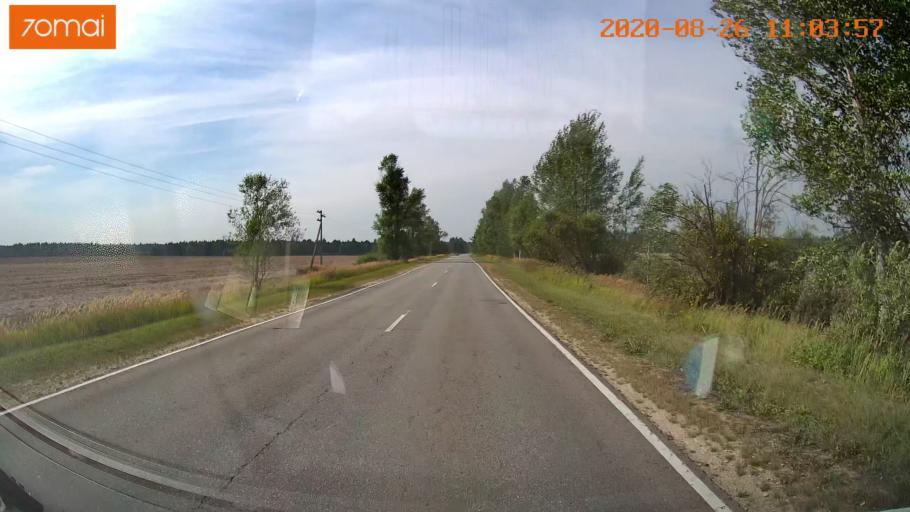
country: RU
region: Rjazan
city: Izhevskoye
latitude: 54.5352
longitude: 41.2035
